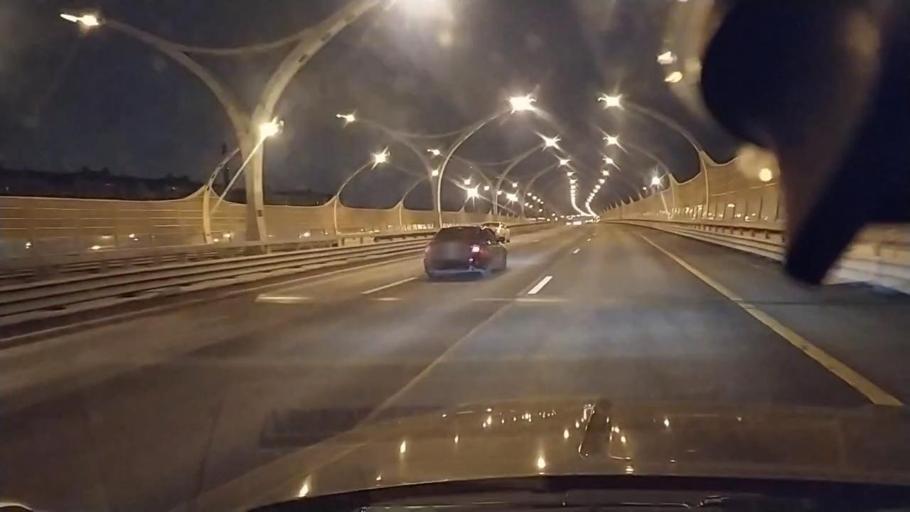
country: RU
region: St.-Petersburg
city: Staraya Derevnya
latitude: 60.0048
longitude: 30.2330
